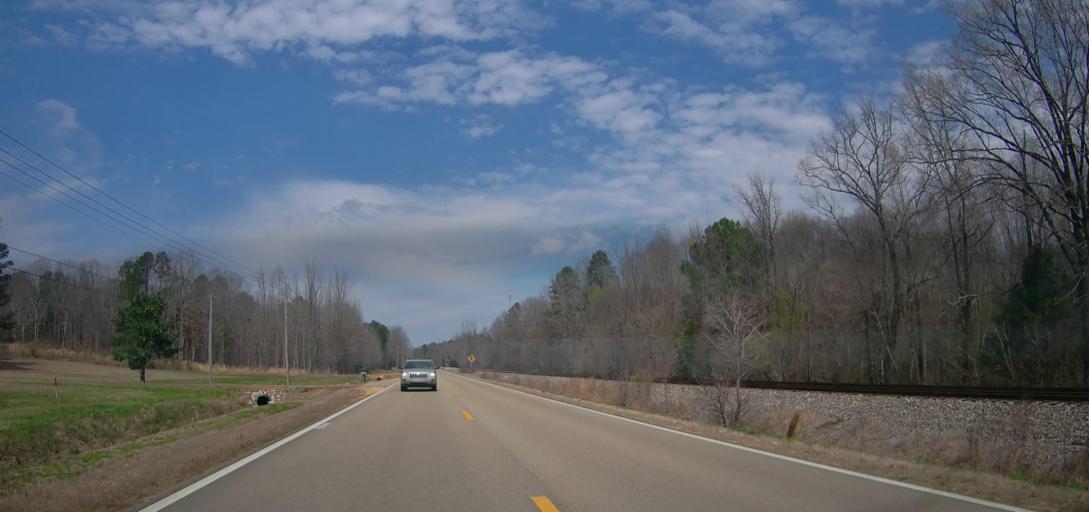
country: US
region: Mississippi
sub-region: Union County
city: New Albany
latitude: 34.5920
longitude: -89.1353
